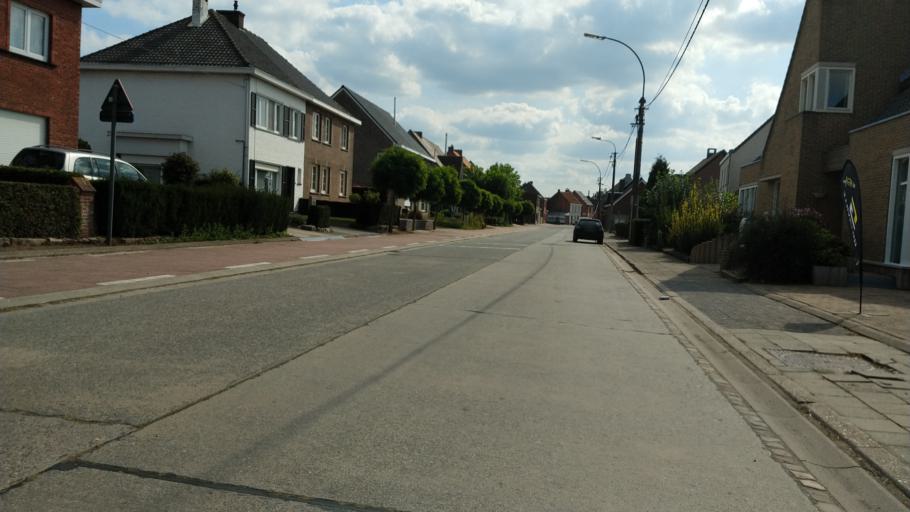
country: BE
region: Flanders
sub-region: Provincie Oost-Vlaanderen
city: Kaprijke
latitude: 51.2277
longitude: 3.6747
